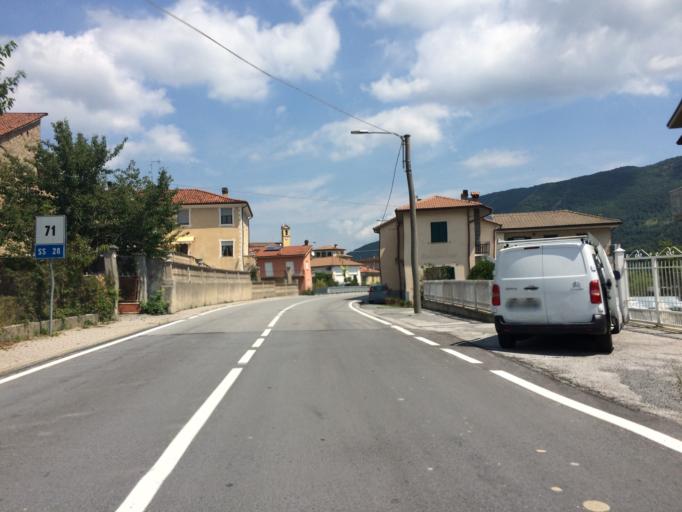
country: IT
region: Piedmont
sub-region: Provincia di Cuneo
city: Priola
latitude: 44.2575
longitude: 8.0213
